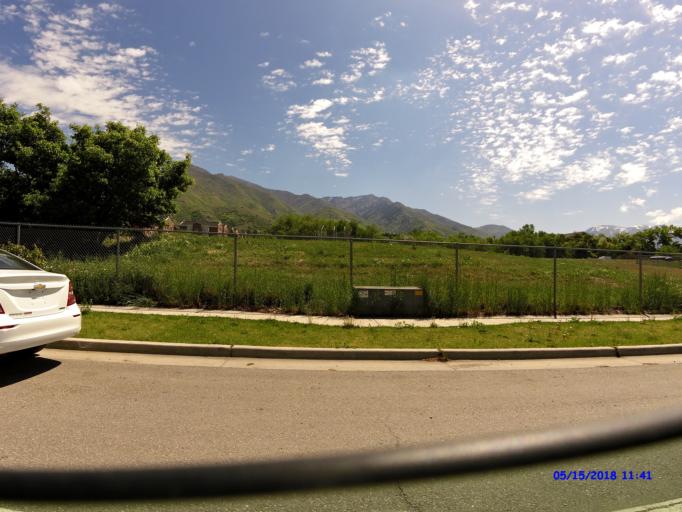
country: US
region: Utah
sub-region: Weber County
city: South Ogden
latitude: 41.1777
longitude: -111.9477
